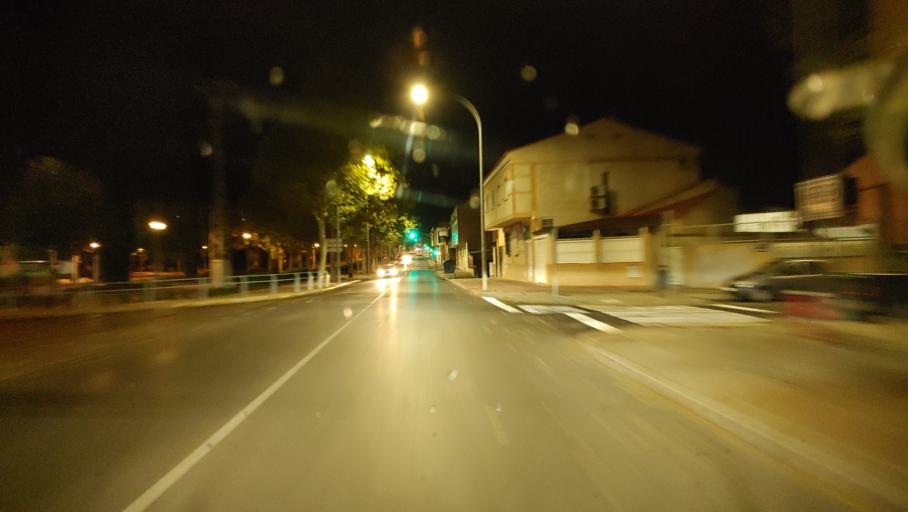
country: ES
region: Castille-La Mancha
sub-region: Provincia de Ciudad Real
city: Ciudad Real
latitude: 38.9747
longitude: -3.9270
